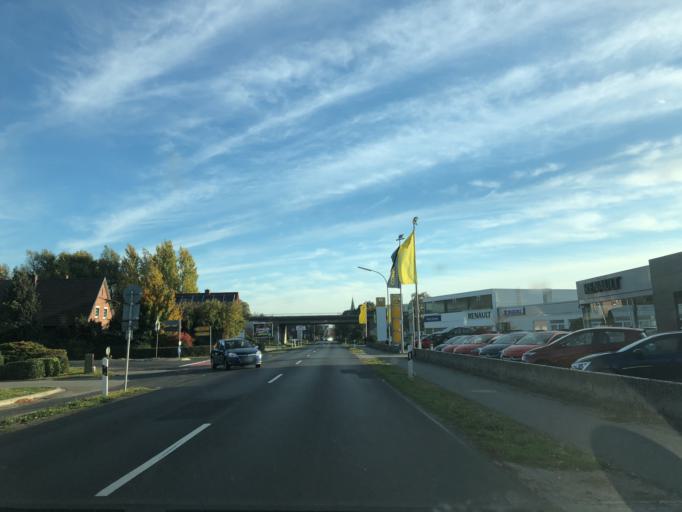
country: DE
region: Lower Saxony
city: Papenburg
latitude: 53.0735
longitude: 7.3823
